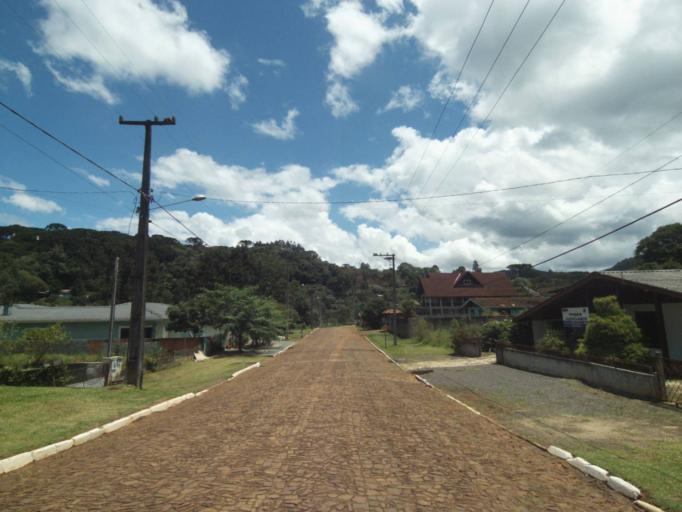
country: BR
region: Parana
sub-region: Uniao Da Vitoria
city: Uniao da Vitoria
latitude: -26.1667
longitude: -51.5573
